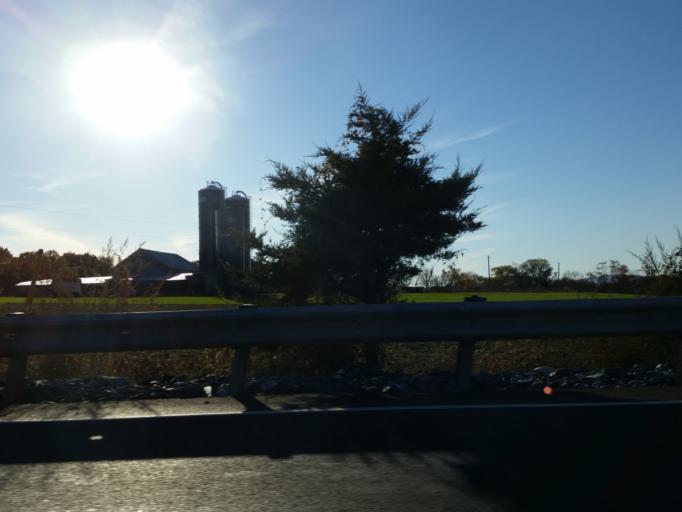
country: US
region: Pennsylvania
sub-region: Lebanon County
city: Annville
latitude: 40.3811
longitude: -76.5564
